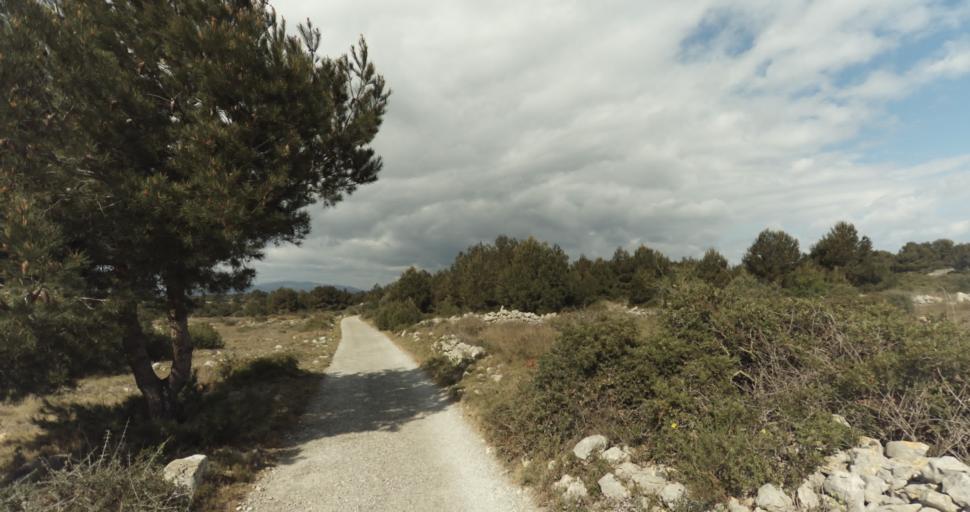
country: FR
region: Languedoc-Roussillon
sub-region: Departement de l'Aude
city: Leucate
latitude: 42.9184
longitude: 3.0521
